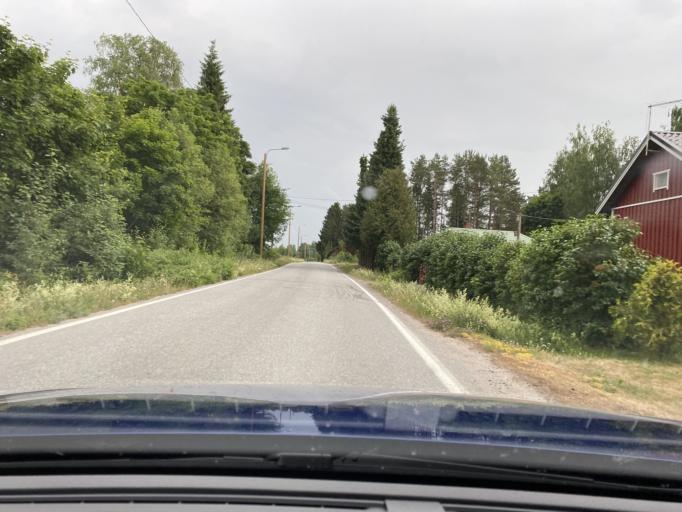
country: FI
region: Satakunta
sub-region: Rauma
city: Eura
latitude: 61.1490
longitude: 22.1234
